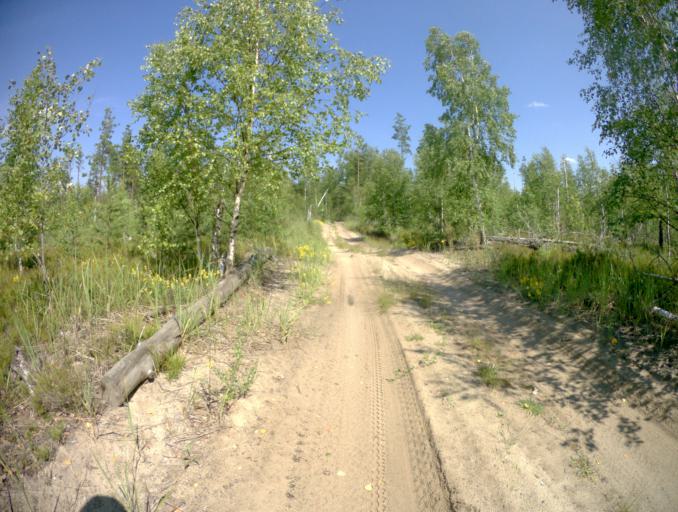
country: RU
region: Ivanovo
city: Talitsy
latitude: 56.4748
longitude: 42.2253
